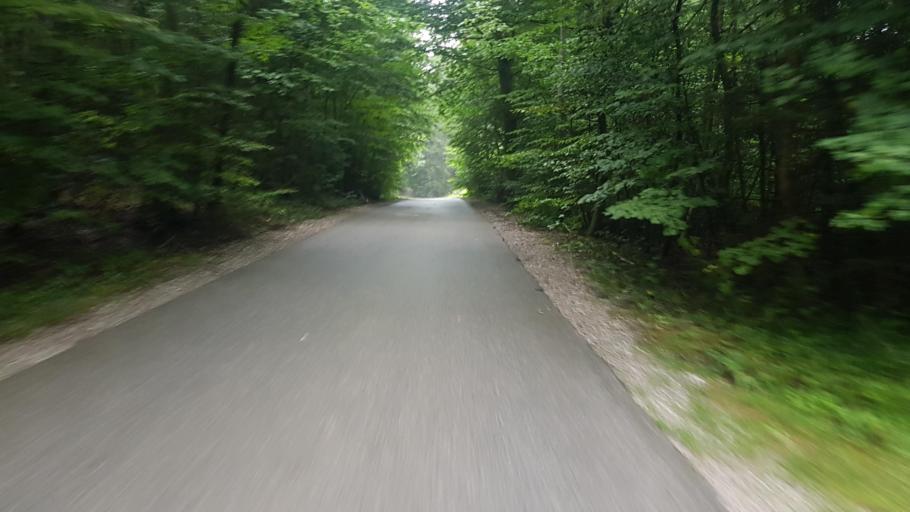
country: DE
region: Bavaria
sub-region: Upper Bavaria
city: Starnberg
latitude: 48.0175
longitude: 11.3466
